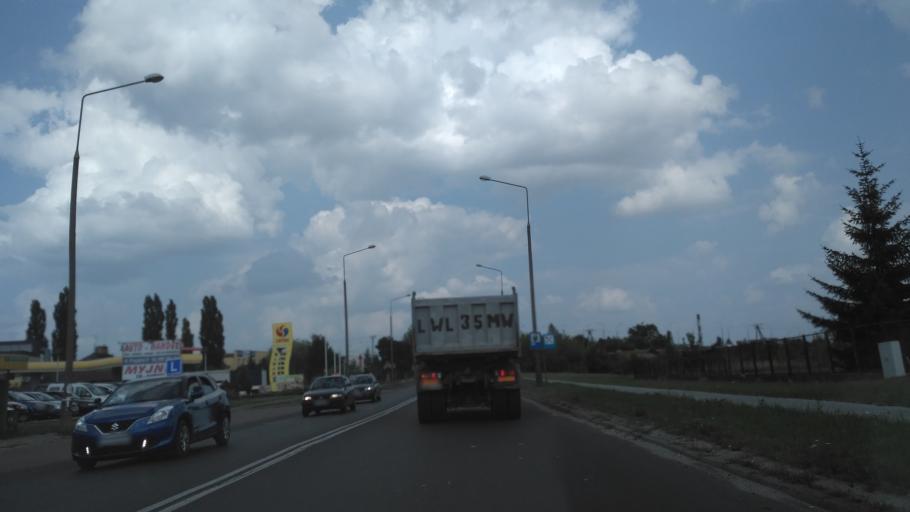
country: PL
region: Lublin Voivodeship
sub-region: Chelm
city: Chelm
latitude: 51.1435
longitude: 23.4744
